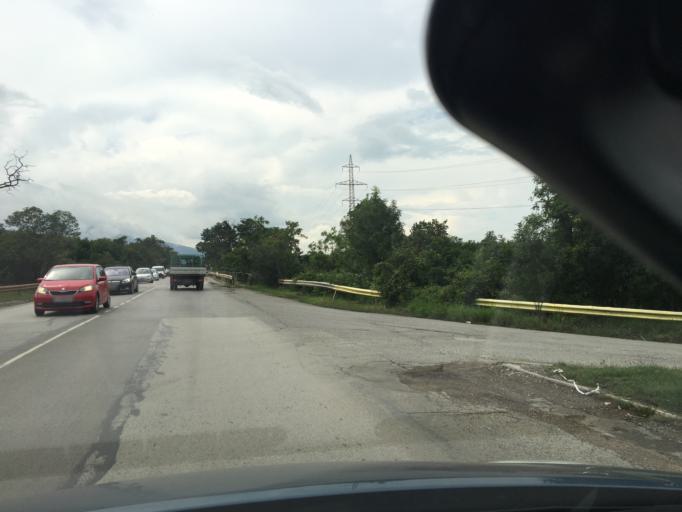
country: BG
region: Sofia-Capital
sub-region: Stolichna Obshtina
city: Sofia
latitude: 42.6229
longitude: 23.3940
